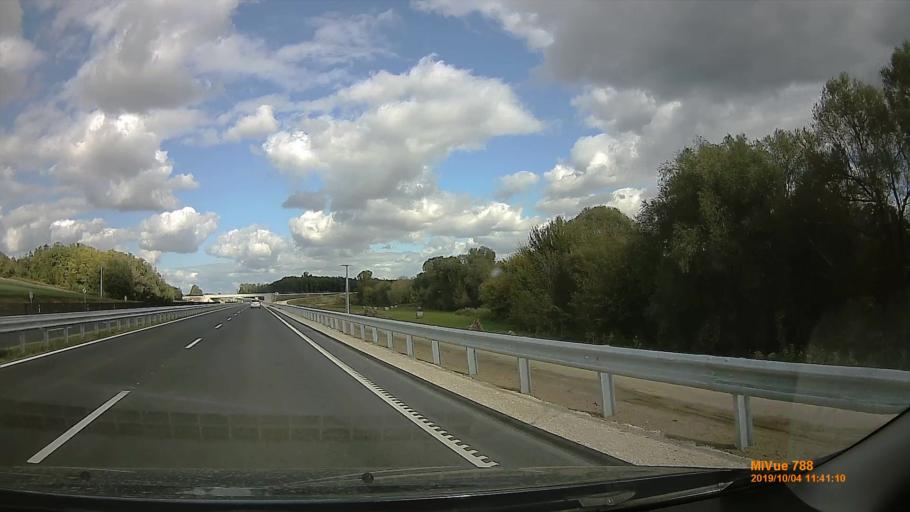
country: HU
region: Somogy
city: Karad
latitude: 46.5741
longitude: 17.8064
